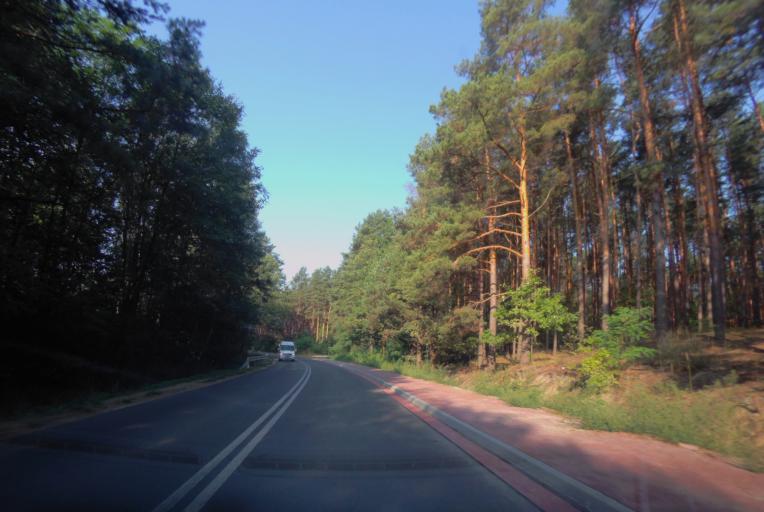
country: PL
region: Subcarpathian Voivodeship
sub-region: Powiat nizanski
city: Jarocin
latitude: 50.5151
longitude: 22.3479
